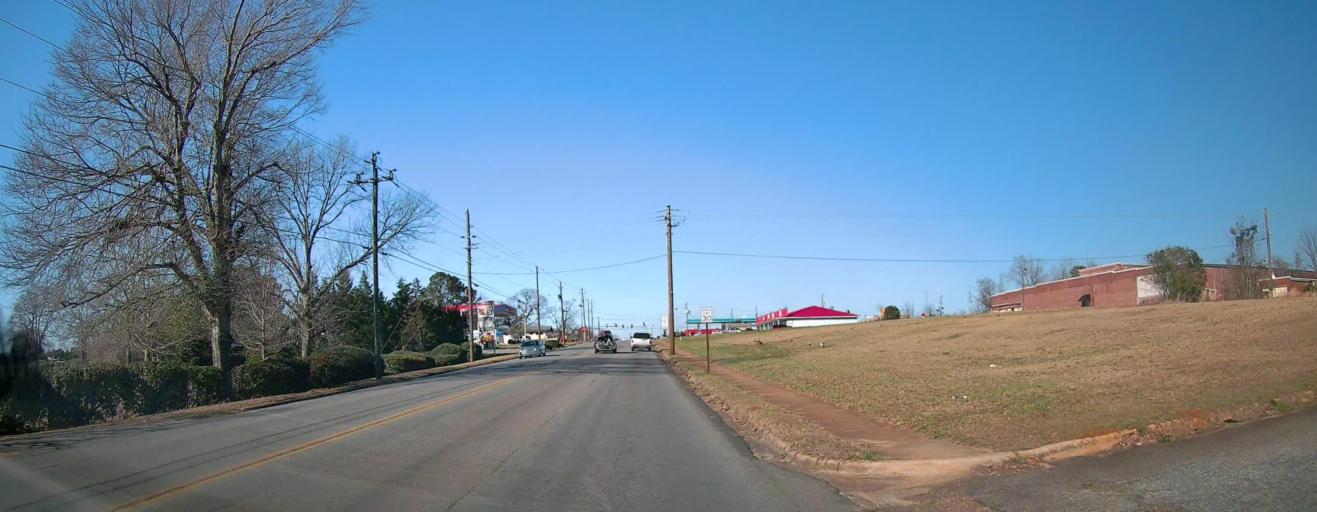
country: US
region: Georgia
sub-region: Sumter County
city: Americus
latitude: 32.0688
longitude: -84.2175
